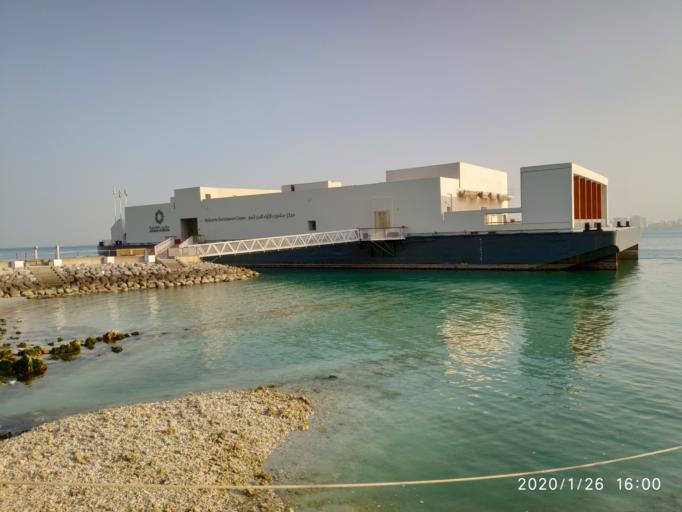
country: QA
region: Baladiyat ad Dawhah
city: Doha
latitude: 25.3165
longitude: 51.5309
